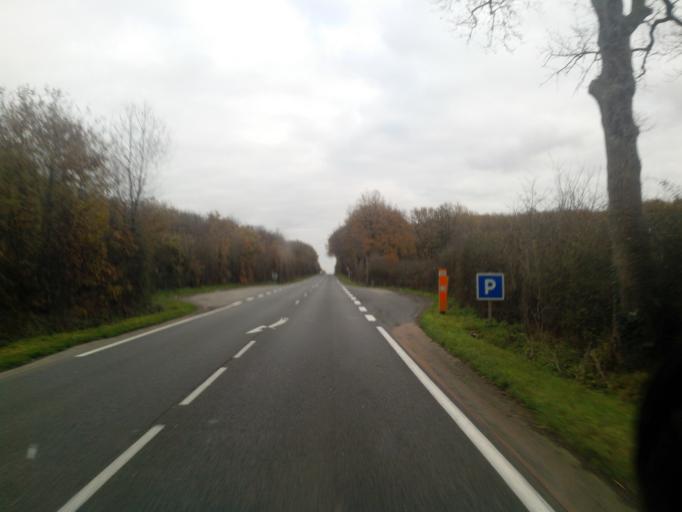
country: FR
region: Poitou-Charentes
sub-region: Departement des Deux-Sevres
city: Chiche
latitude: 46.8129
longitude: -0.3928
